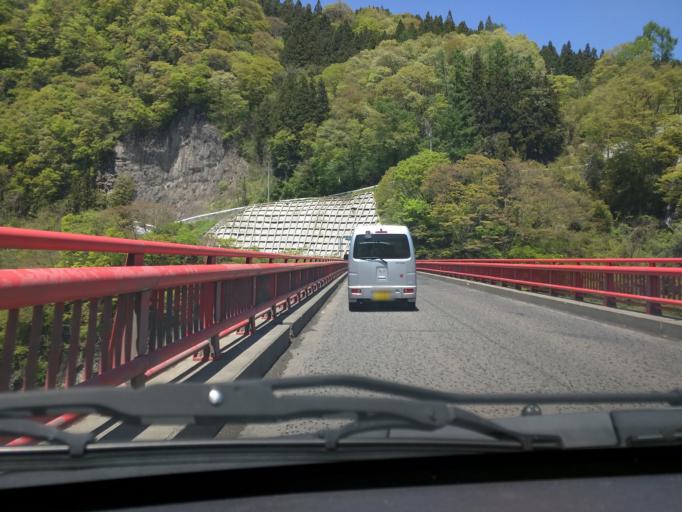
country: JP
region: Nagano
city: Nagano-shi
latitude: 36.6684
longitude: 138.1142
